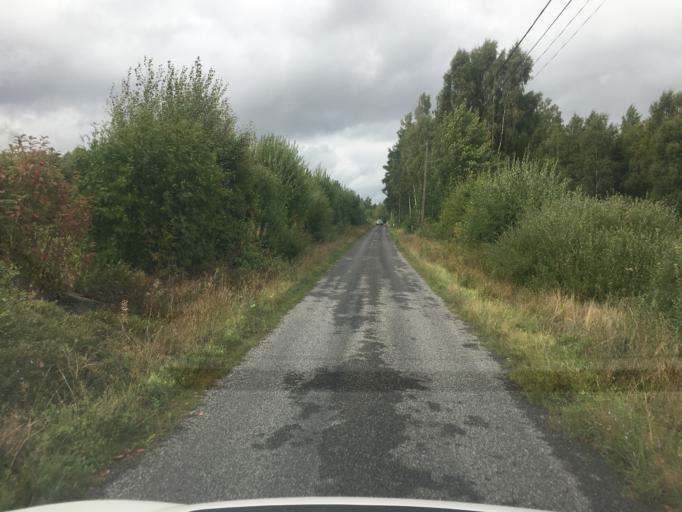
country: SE
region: Kronoberg
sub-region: Ljungby Kommun
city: Lagan
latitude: 56.9338
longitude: 14.0255
